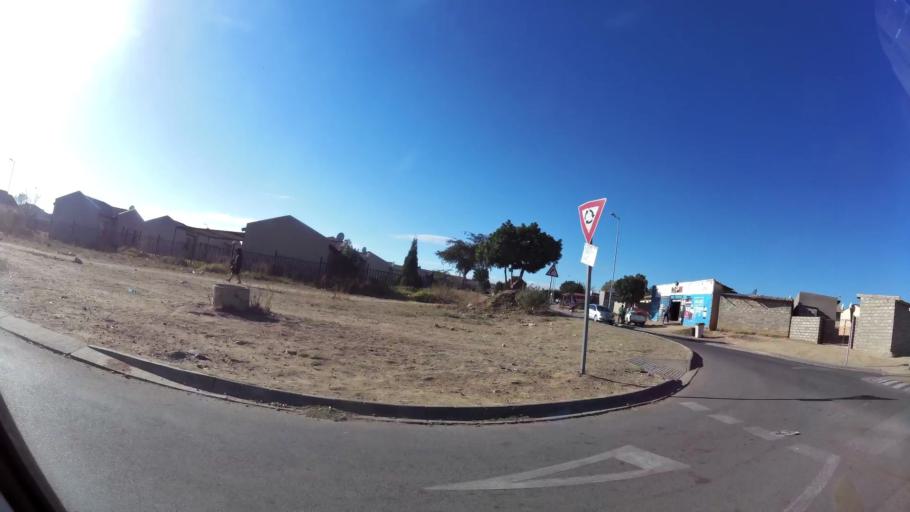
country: ZA
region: Gauteng
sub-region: City of Johannesburg Metropolitan Municipality
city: Diepsloot
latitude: -25.8968
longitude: 28.0955
